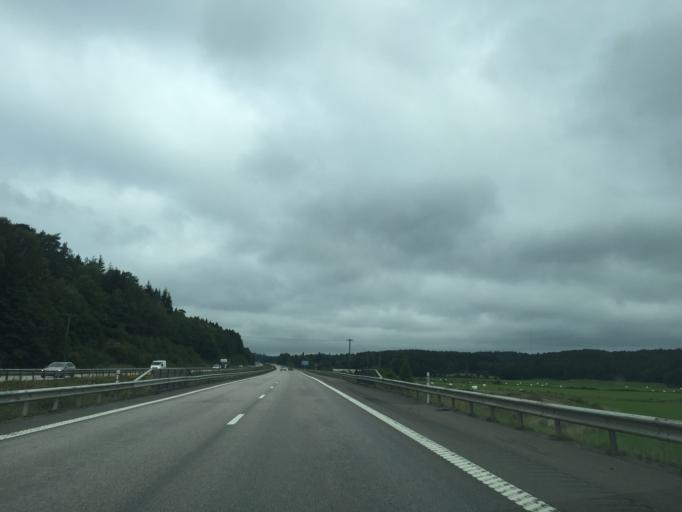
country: SE
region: Halland
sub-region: Kungsbacka Kommun
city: Frillesas
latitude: 57.3656
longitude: 12.2058
